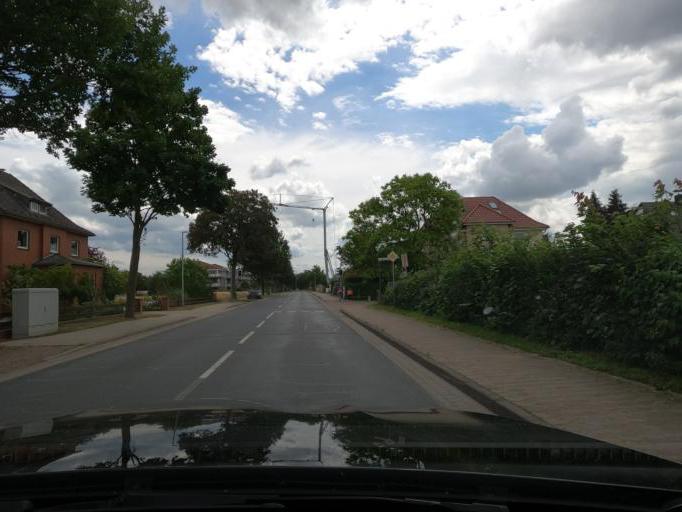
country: DE
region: Lower Saxony
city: Sehnde
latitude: 52.3508
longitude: 9.8978
